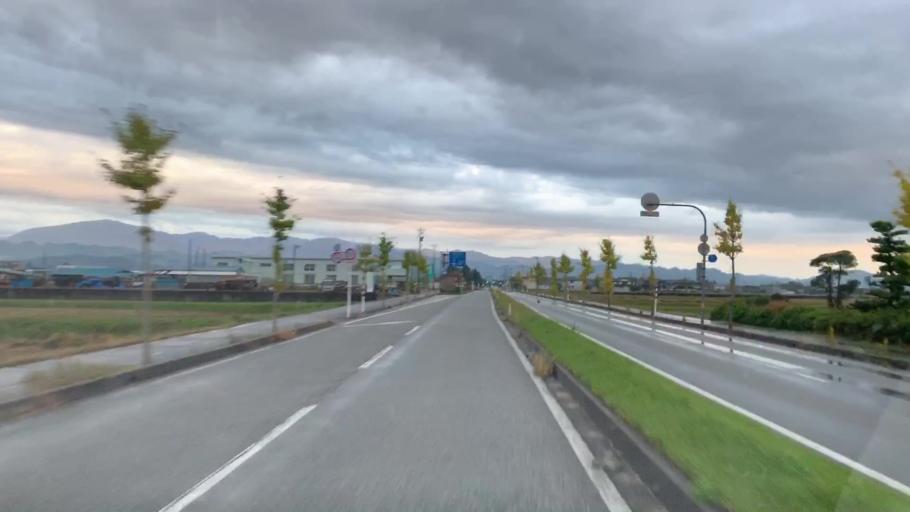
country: JP
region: Toyama
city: Kamiichi
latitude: 36.6728
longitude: 137.3275
